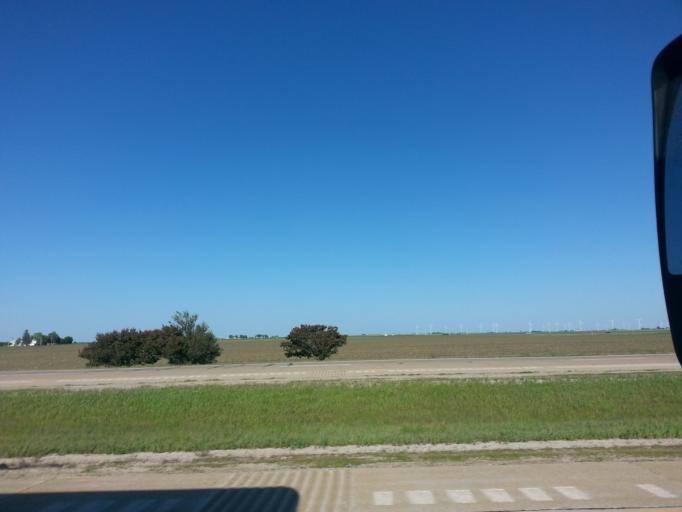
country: US
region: Illinois
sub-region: Woodford County
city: Minonk
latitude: 40.9370
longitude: -89.0568
